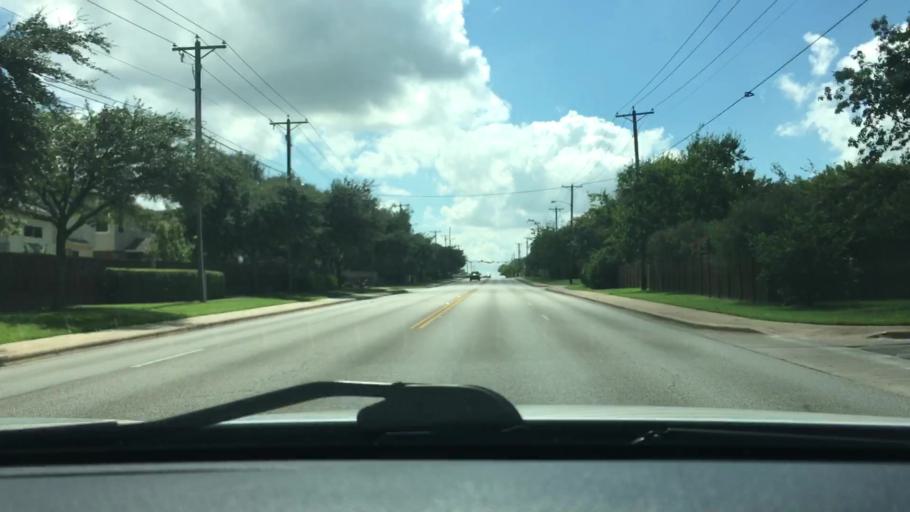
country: US
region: Texas
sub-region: Williamson County
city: Round Rock
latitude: 30.5333
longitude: -97.6680
